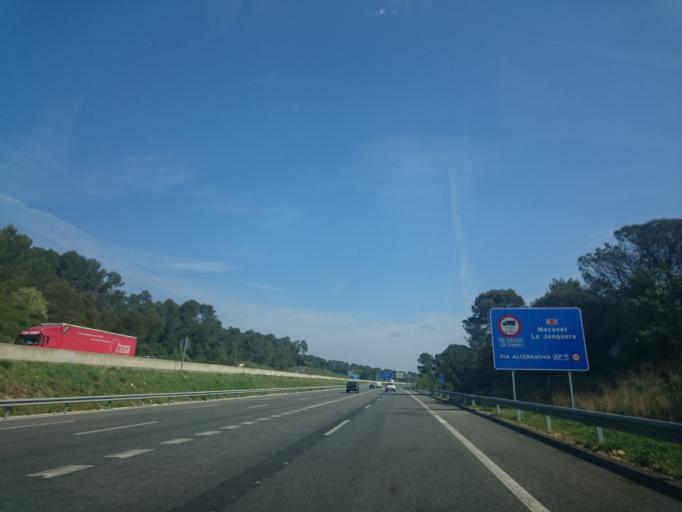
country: ES
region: Catalonia
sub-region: Provincia de Girona
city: Cervia de Ter
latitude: 42.0674
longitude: 2.8869
